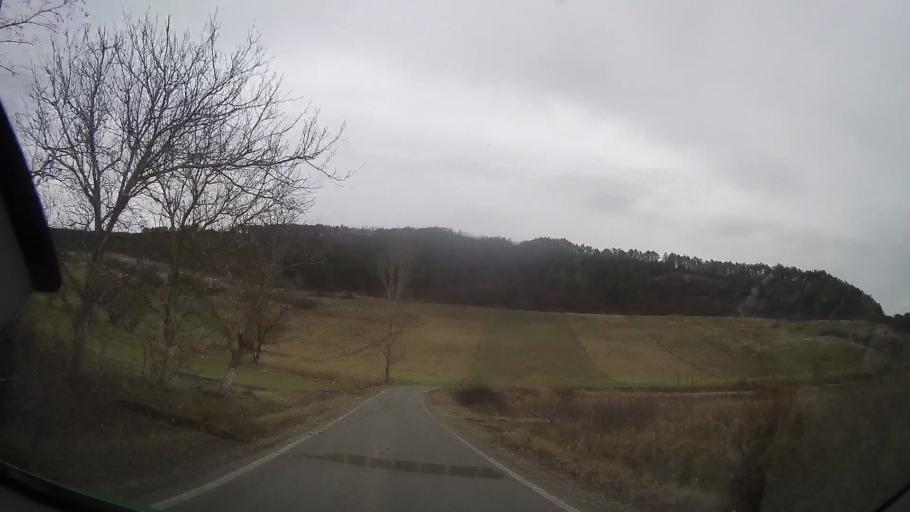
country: RO
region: Mures
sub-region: Comuna Bala
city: Bala
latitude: 46.7153
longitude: 24.5233
